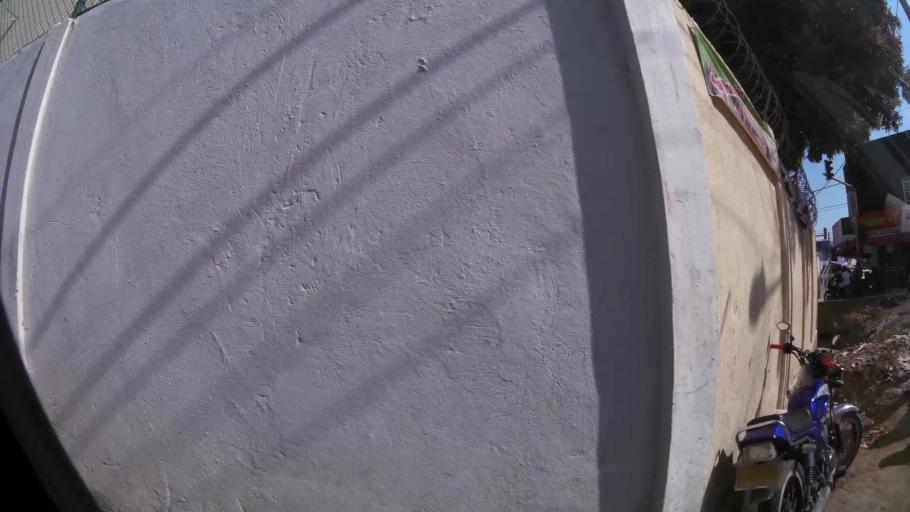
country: CO
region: Bolivar
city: Cartagena
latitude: 10.3969
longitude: -75.4956
